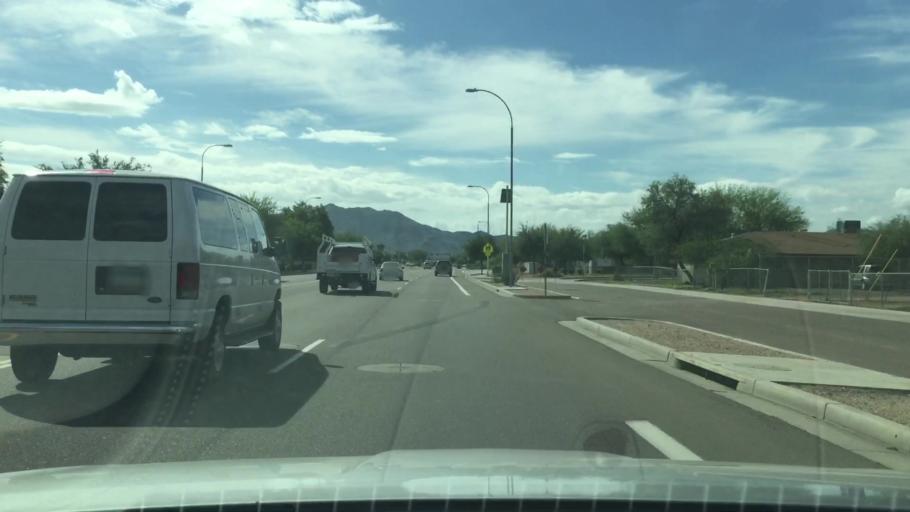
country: US
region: Arizona
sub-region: Maricopa County
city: Laveen
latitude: 33.3963
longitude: -112.1337
